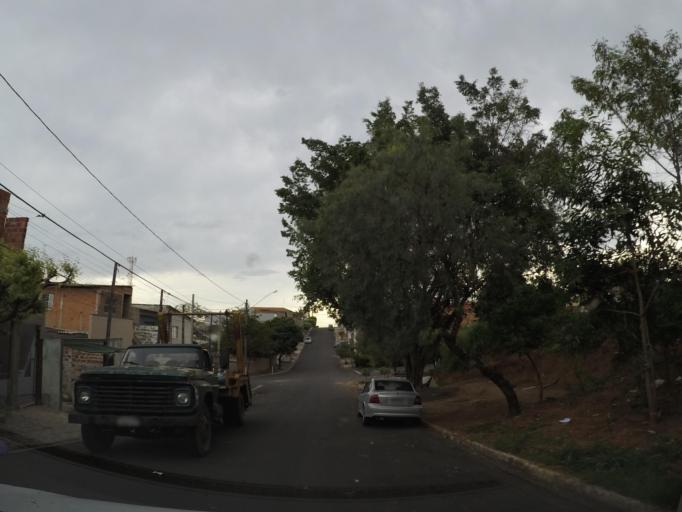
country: BR
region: Sao Paulo
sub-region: Sumare
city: Sumare
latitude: -22.8154
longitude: -47.2481
